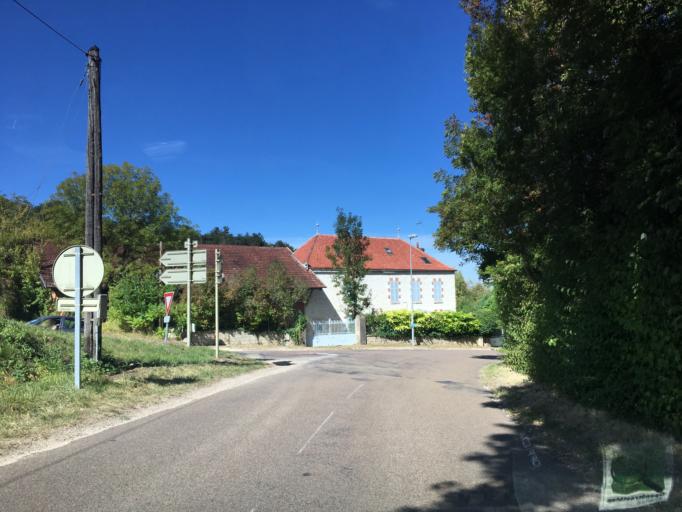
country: FR
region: Bourgogne
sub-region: Departement de l'Yonne
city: Vermenton
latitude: 47.5938
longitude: 3.6798
